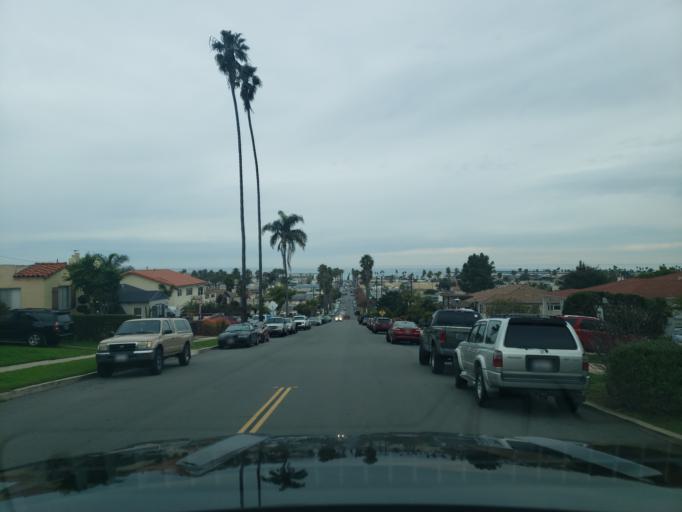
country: US
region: California
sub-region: San Diego County
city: Coronado
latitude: 32.7427
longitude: -117.2443
